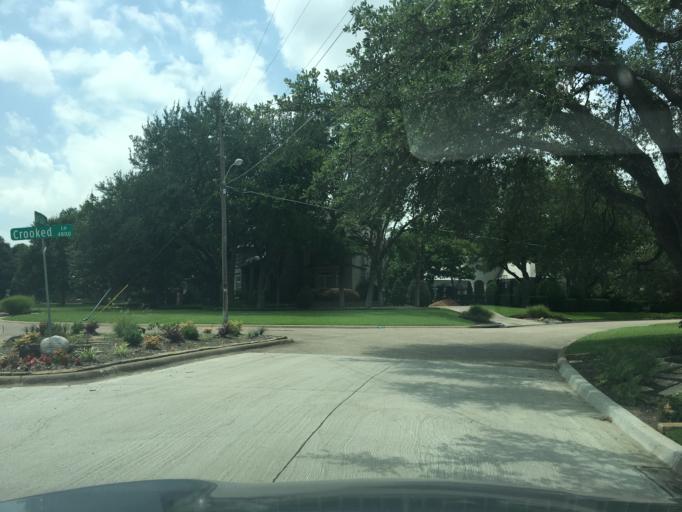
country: US
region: Texas
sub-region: Dallas County
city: University Park
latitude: 32.9001
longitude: -96.8249
